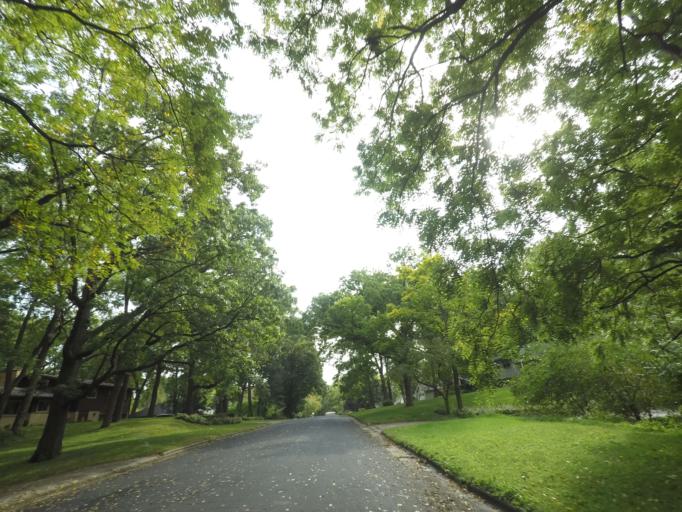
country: US
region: Wisconsin
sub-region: Dane County
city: Shorewood Hills
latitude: 43.0379
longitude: -89.4754
